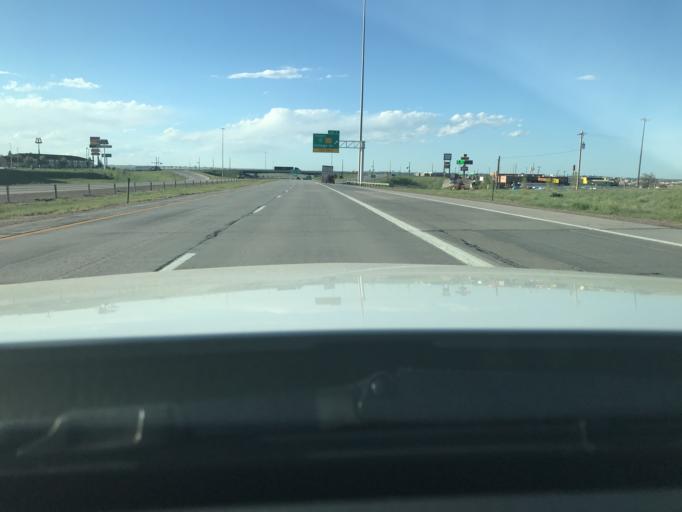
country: US
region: Wyoming
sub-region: Laramie County
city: South Greeley
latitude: 41.0949
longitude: -104.8501
